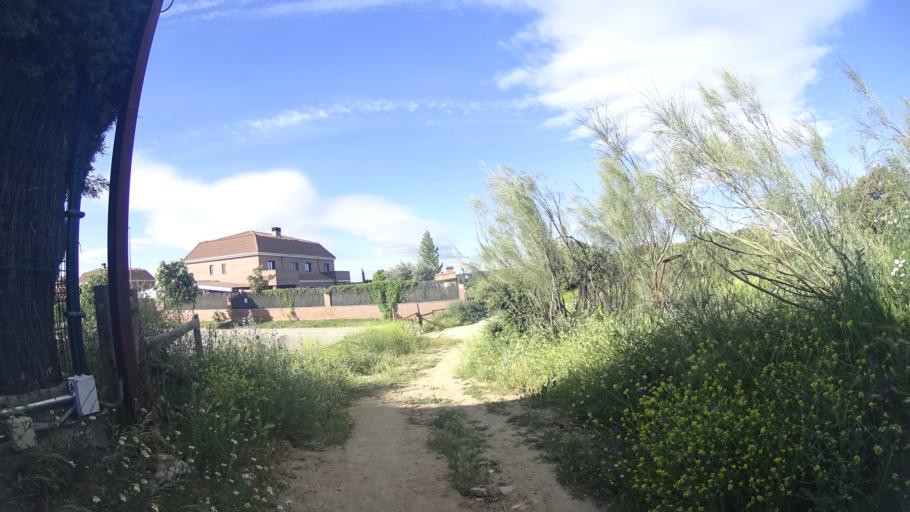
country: ES
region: Madrid
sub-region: Provincia de Madrid
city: Torrelodones
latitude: 40.5271
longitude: -3.9354
